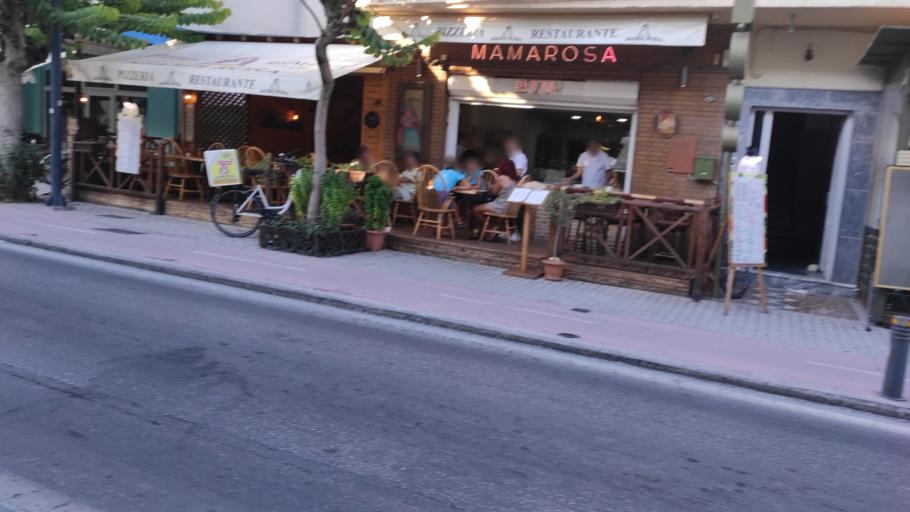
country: GR
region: South Aegean
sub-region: Nomos Dodekanisou
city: Kos
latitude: 36.8998
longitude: 27.2835
